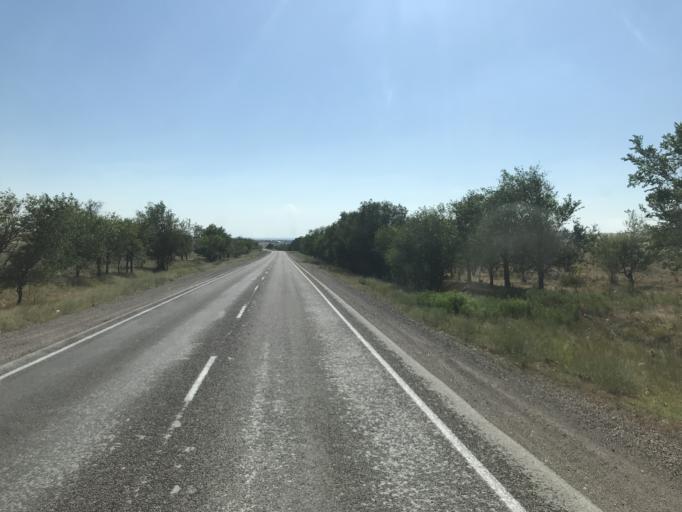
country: KZ
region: Zhambyl
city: Georgiyevka
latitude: 43.2486
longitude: 74.7952
